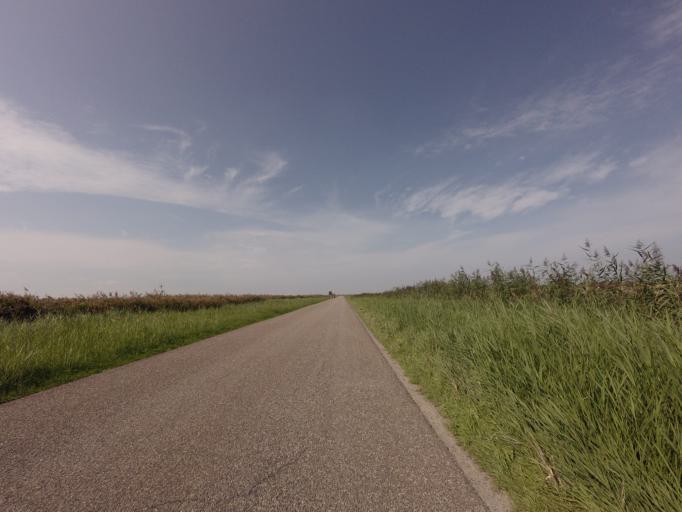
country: NL
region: Groningen
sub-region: Gemeente De Marne
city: Ulrum
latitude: 53.3434
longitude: 6.2813
